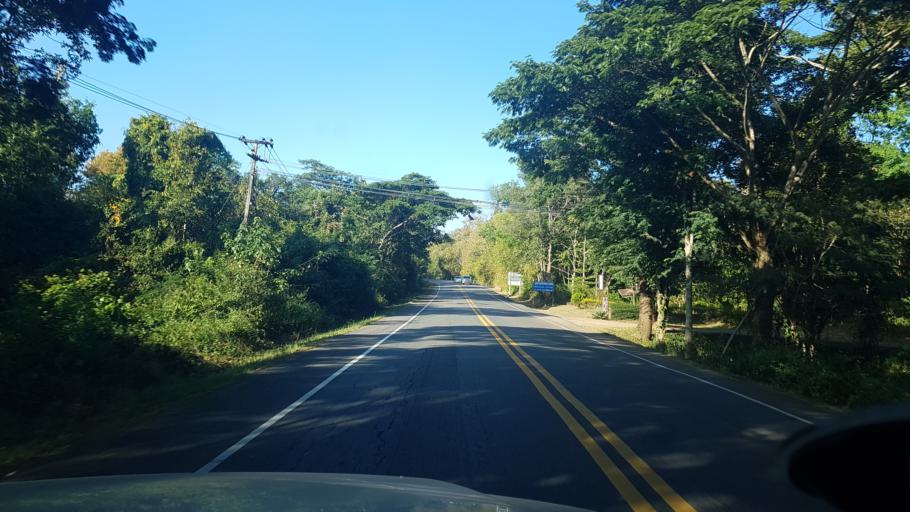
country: TH
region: Phetchabun
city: Nam Nao
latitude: 16.7594
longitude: 101.4692
